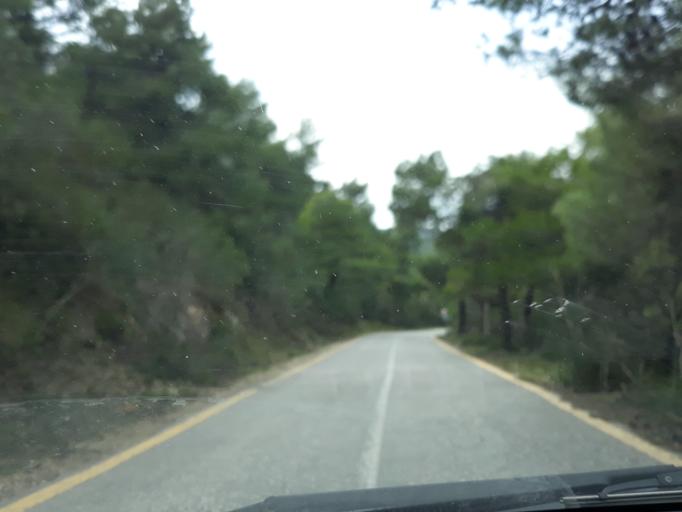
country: GR
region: Attica
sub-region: Nomarchia Anatolikis Attikis
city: Afidnes
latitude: 38.1881
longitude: 23.7875
